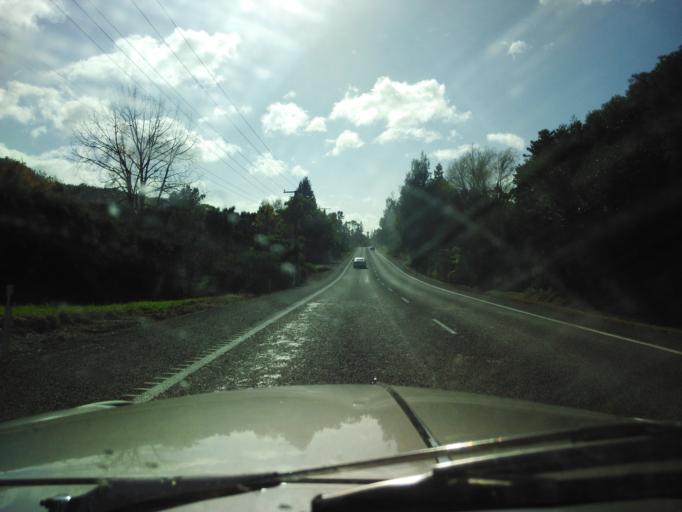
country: NZ
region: Bay of Plenty
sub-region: Western Bay of Plenty District
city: Katikati
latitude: -37.4870
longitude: 175.9295
